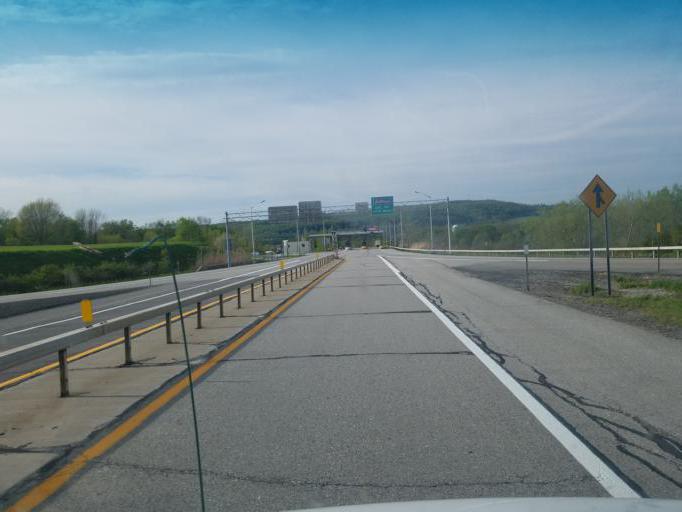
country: US
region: New York
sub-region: Herkimer County
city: Little Falls
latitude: 43.0178
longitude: -74.8180
